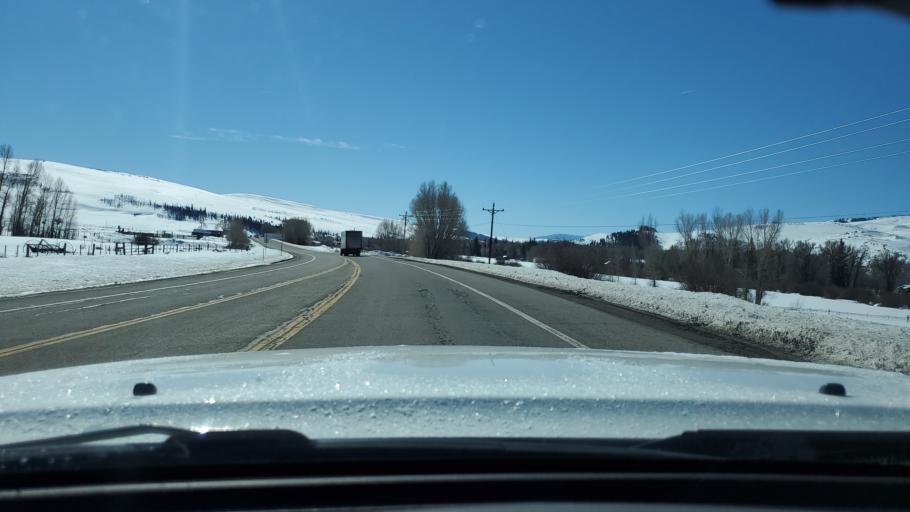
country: US
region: Colorado
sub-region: Gunnison County
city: Crested Butte
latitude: 38.7395
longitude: -106.8563
